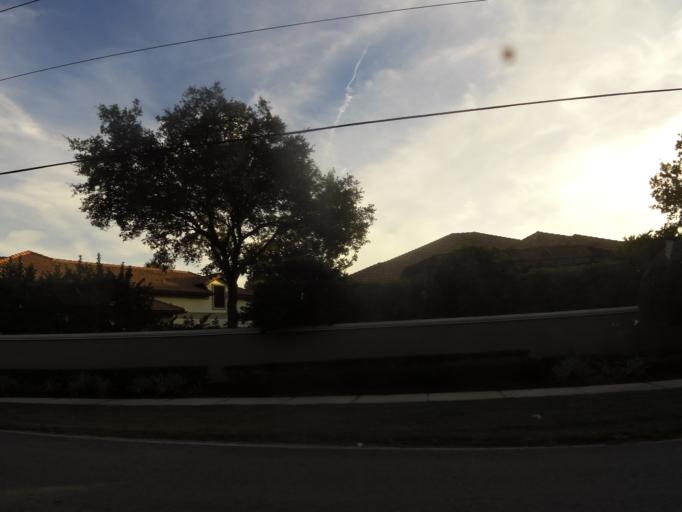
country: US
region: Florida
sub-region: Saint Johns County
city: Palm Valley
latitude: 30.1771
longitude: -81.3882
